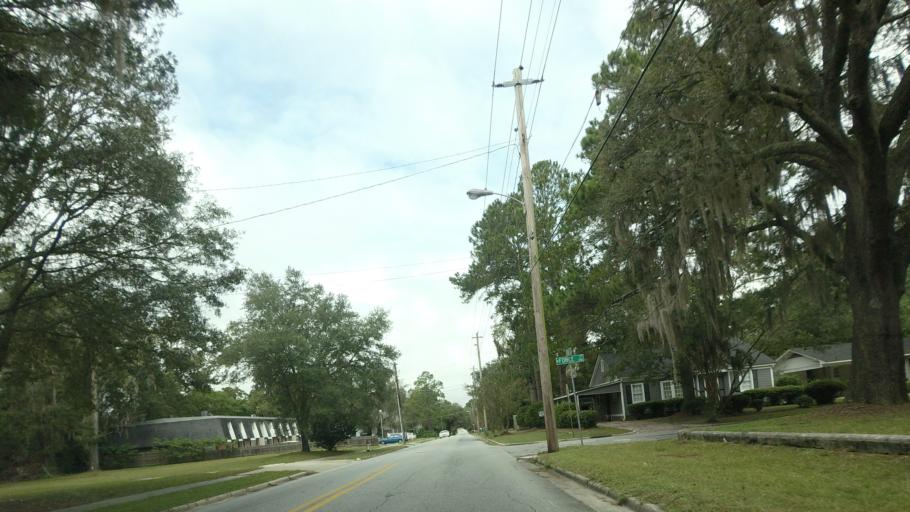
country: US
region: Georgia
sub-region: Lowndes County
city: Valdosta
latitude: 30.8394
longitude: -83.2865
